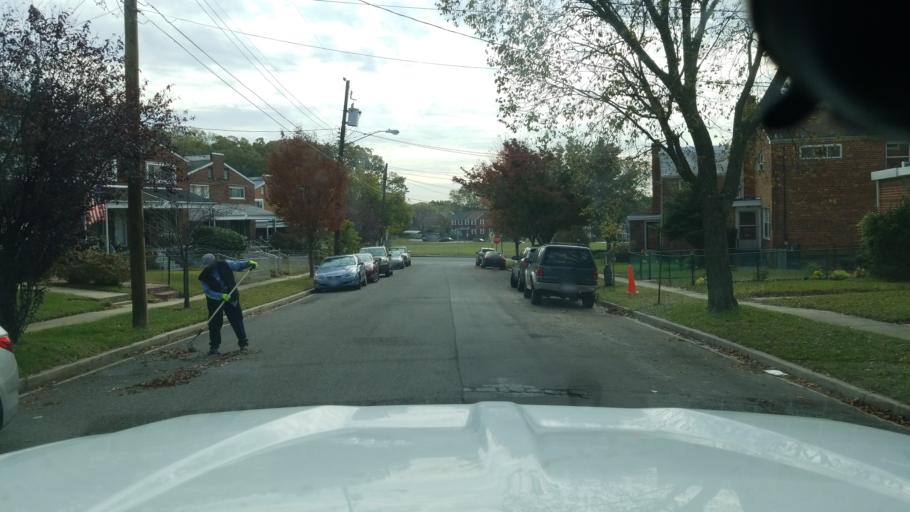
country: US
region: Maryland
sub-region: Prince George's County
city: Chillum
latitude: 38.9537
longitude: -76.9952
